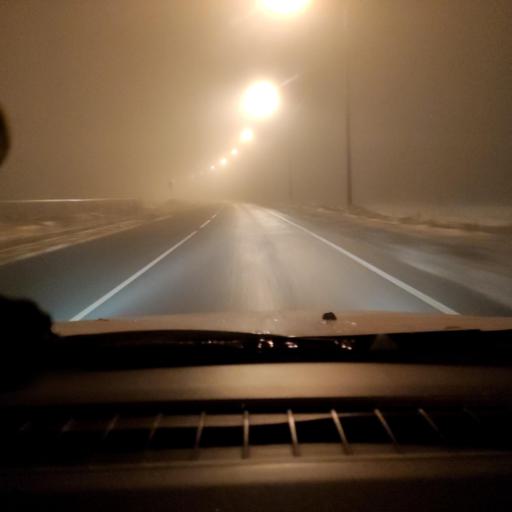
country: RU
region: Samara
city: Dubovyy Umet
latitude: 52.9680
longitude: 50.2806
